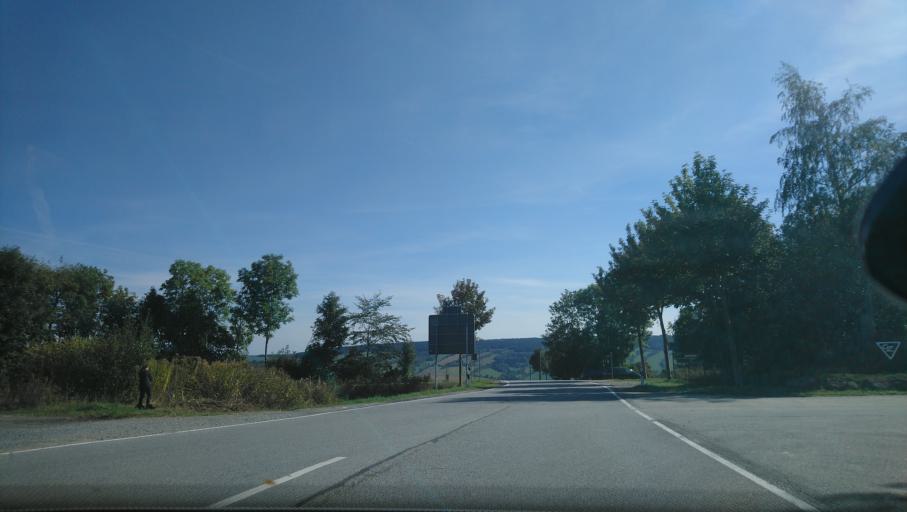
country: DE
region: Saxony
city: Konigswalde
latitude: 50.5494
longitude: 13.0191
